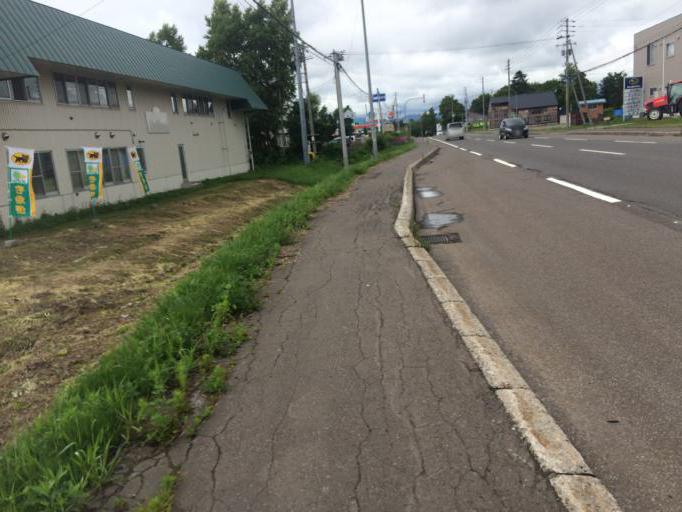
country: JP
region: Hokkaido
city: Niseko Town
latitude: 42.8711
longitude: 140.7490
